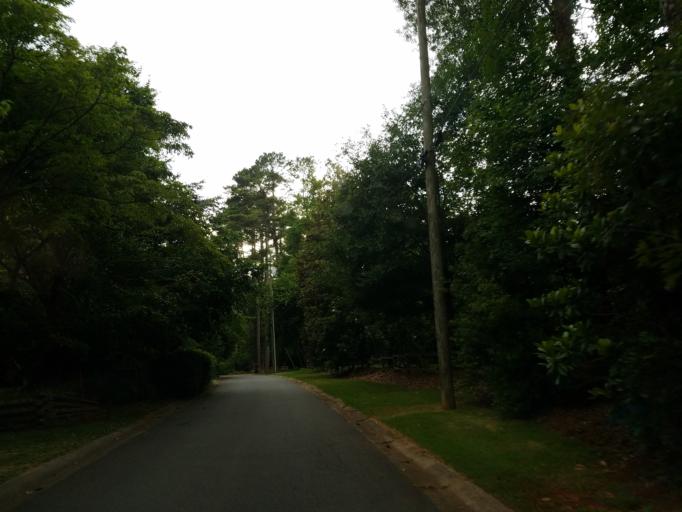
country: US
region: Georgia
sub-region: Cobb County
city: Marietta
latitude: 33.9465
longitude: -84.5608
